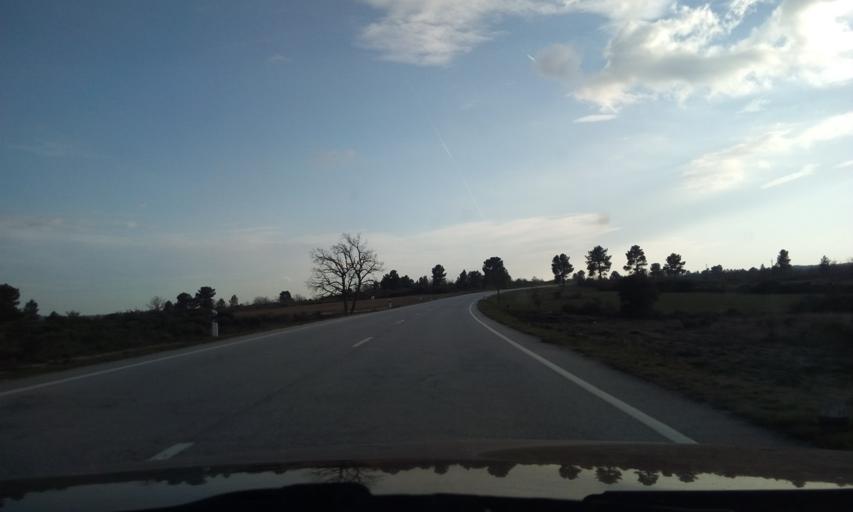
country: ES
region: Castille and Leon
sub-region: Provincia de Salamanca
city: Fuentes de Onoro
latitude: 40.6290
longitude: -6.9734
